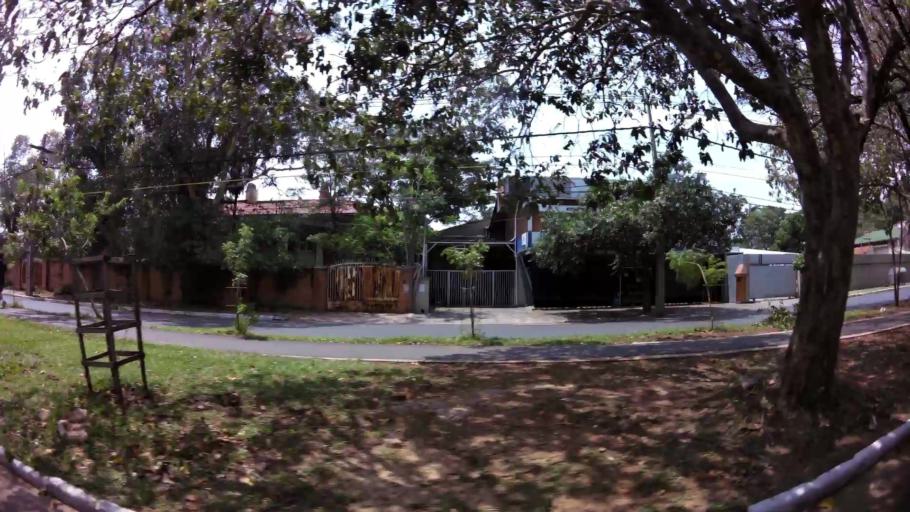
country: PY
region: Central
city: Fernando de la Mora
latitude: -25.3073
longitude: -57.5650
